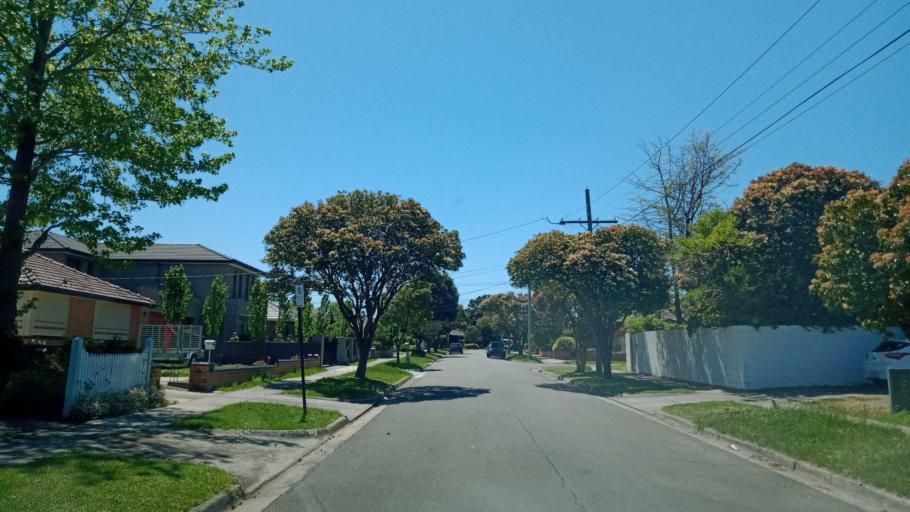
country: AU
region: Victoria
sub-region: Greater Dandenong
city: Springvale
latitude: -37.9292
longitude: 145.1702
